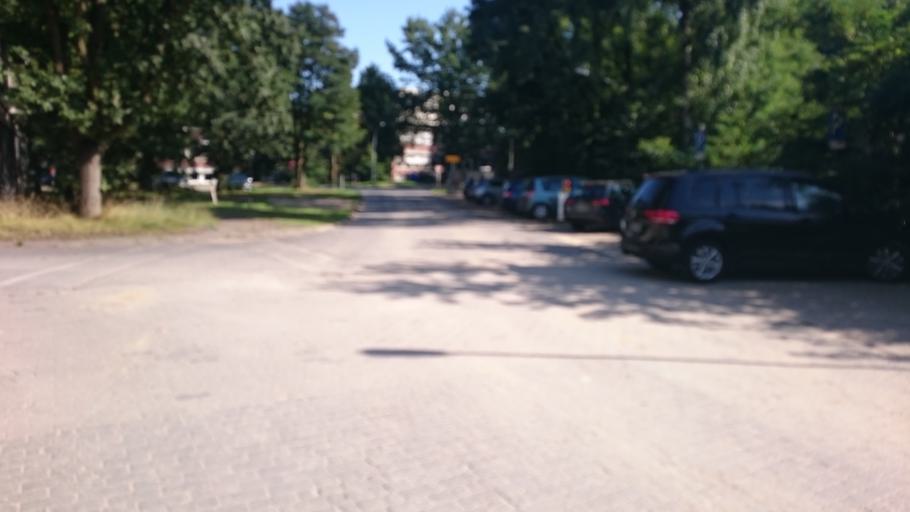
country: DE
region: Hamburg
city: Eidelstedt
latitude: 53.5768
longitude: 9.8766
